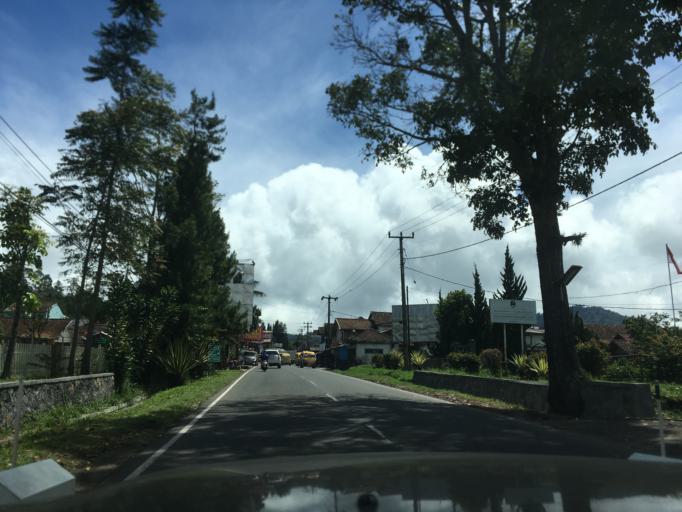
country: ID
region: West Java
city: Lembang
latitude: -6.7989
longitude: 107.6525
